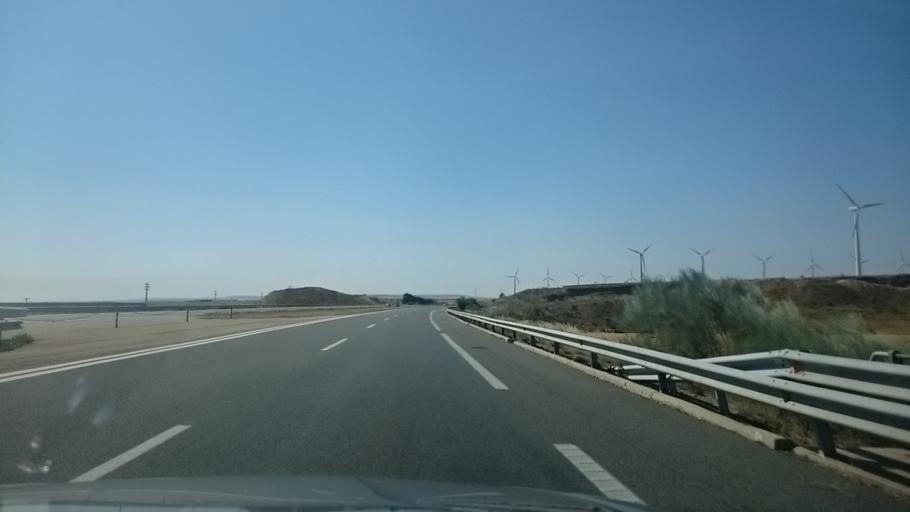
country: ES
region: Aragon
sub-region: Provincia de Zaragoza
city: Luceni
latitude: 41.8046
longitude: -1.2631
